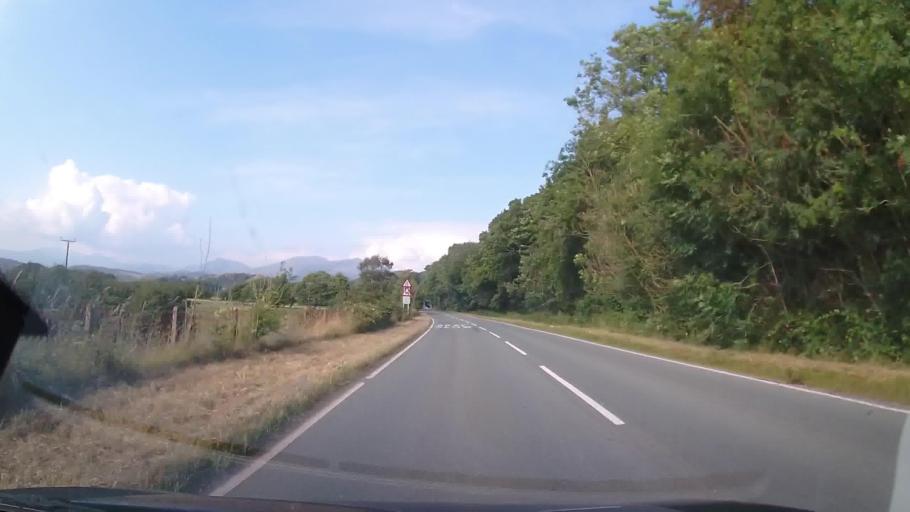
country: GB
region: Wales
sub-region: Gwynedd
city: Penrhyndeudraeth
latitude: 52.9063
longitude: -4.0591
